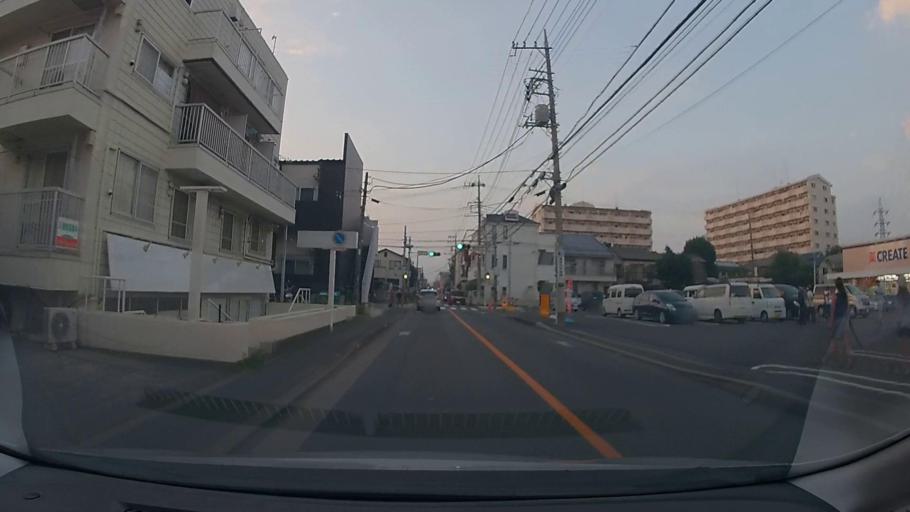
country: JP
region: Kanagawa
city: Minami-rinkan
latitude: 35.5018
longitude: 139.4430
